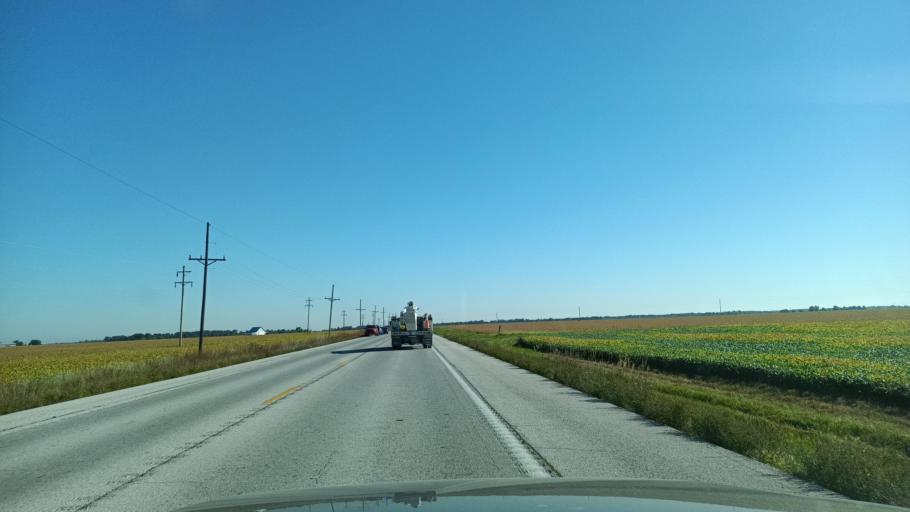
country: US
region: Missouri
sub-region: Audrain County
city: Vandalia
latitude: 39.4730
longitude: -91.5914
